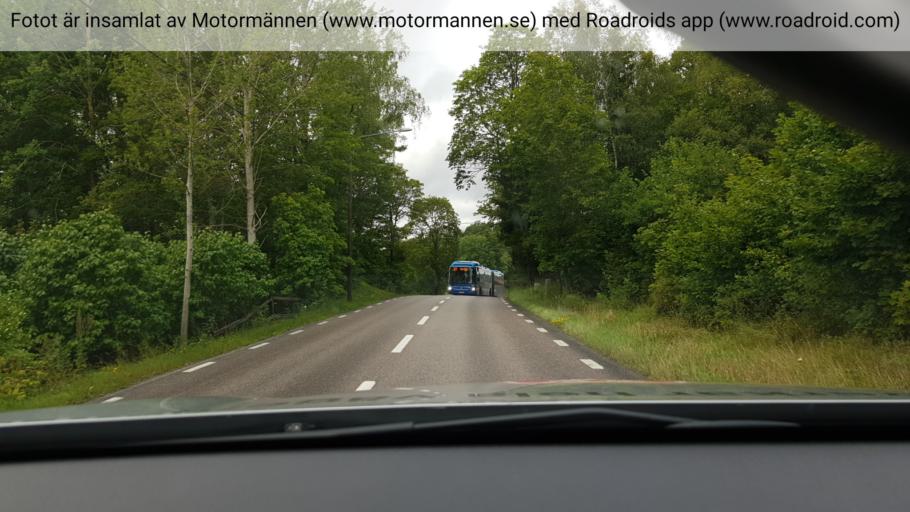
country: SE
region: Stockholm
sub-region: Norrtalje Kommun
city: Rimbo
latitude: 59.7365
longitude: 18.4047
